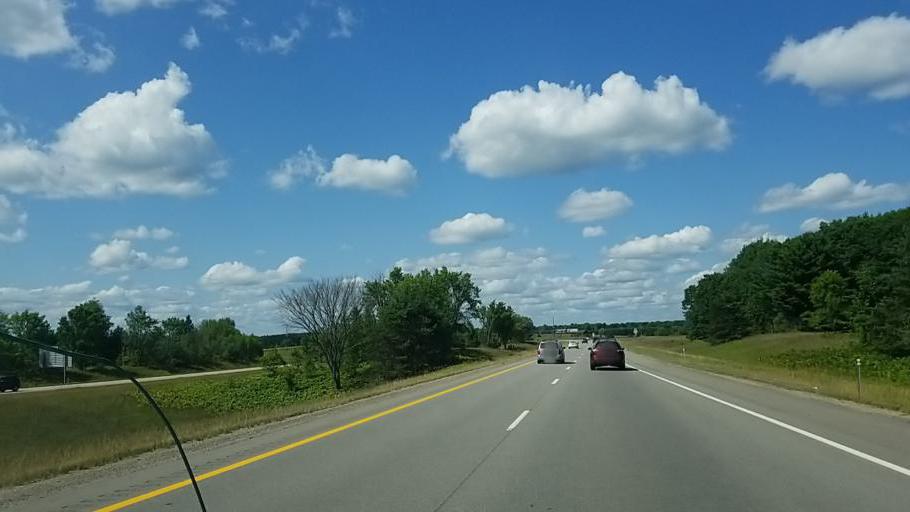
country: US
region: Michigan
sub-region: Mecosta County
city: Big Rapids
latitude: 43.5902
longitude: -85.4877
